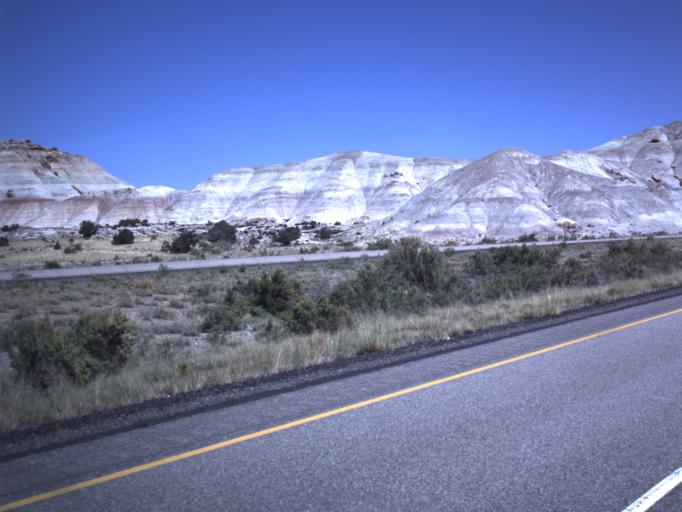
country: US
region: Utah
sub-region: Emery County
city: Ferron
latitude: 38.8167
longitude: -111.1775
